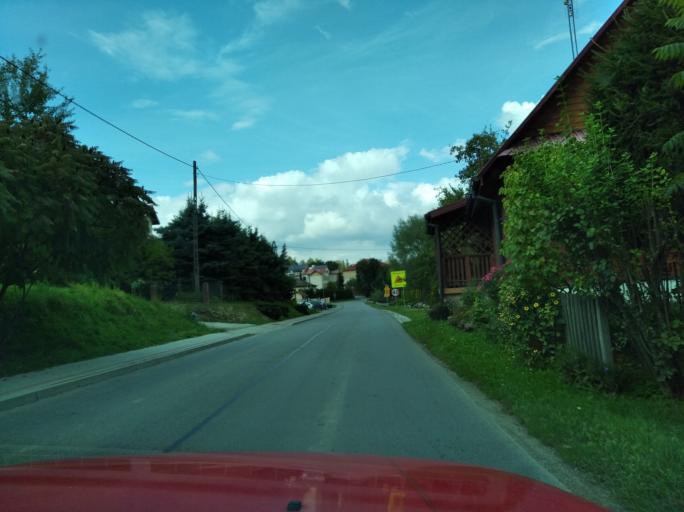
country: PL
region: Subcarpathian Voivodeship
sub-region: Powiat rzeszowski
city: Tyczyn
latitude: 49.9394
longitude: 22.0198
